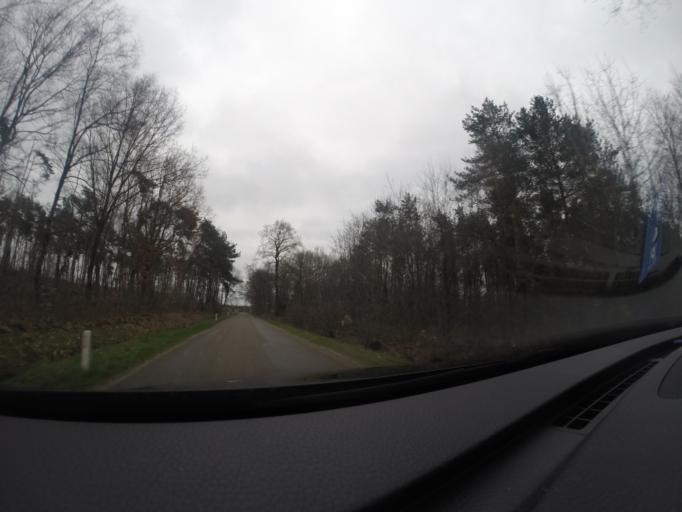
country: NL
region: Overijssel
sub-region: Gemeente Haaksbergen
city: Haaksbergen
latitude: 52.1333
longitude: 6.7286
